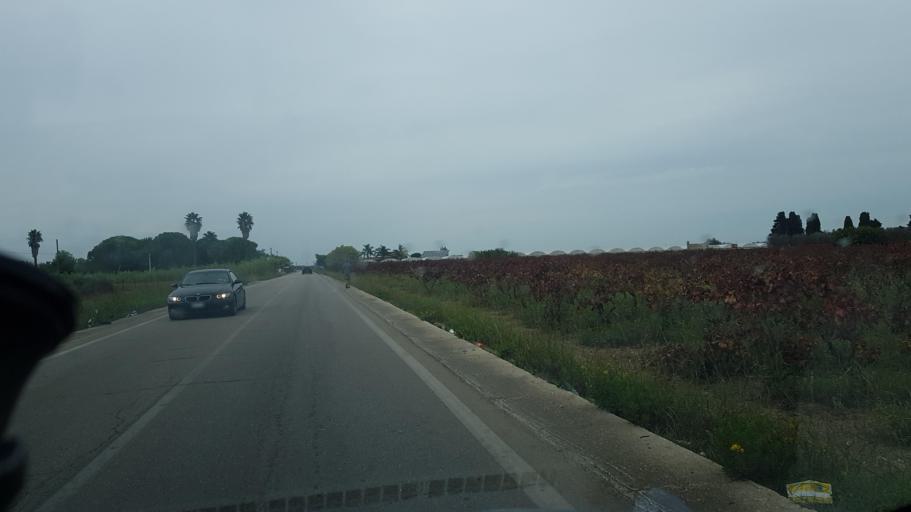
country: IT
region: Apulia
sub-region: Provincia di Lecce
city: Leverano
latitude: 40.3024
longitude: 17.9933
